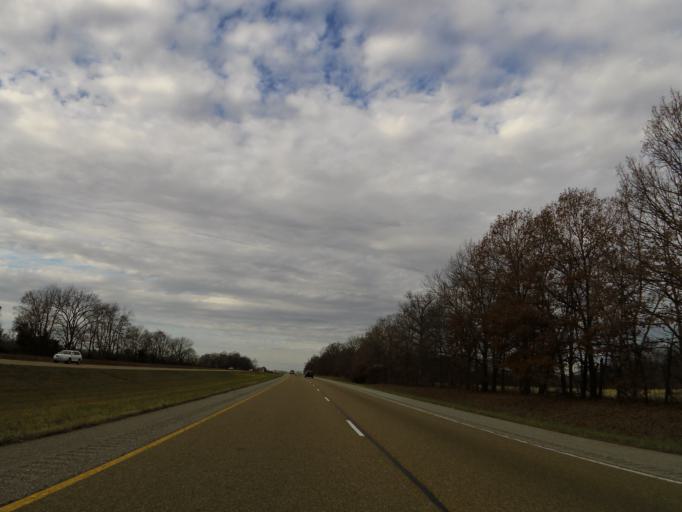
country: US
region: Illinois
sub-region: Clinton County
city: Wamac
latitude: 38.3893
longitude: -89.2063
